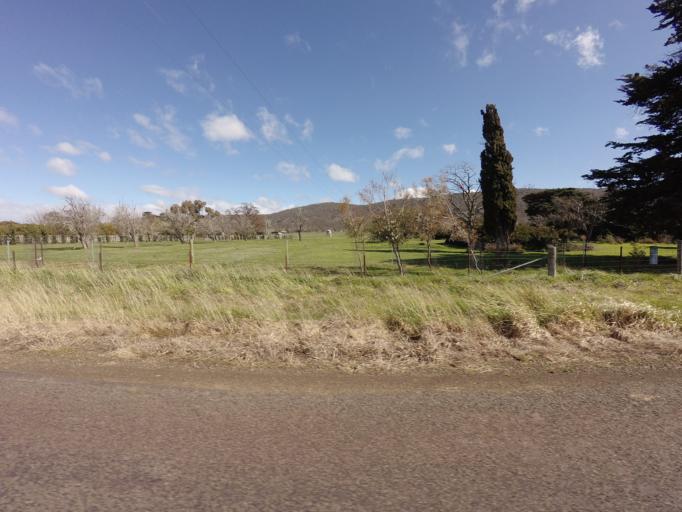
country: AU
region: Tasmania
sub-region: Northern Midlands
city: Evandale
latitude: -41.9821
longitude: 147.4493
